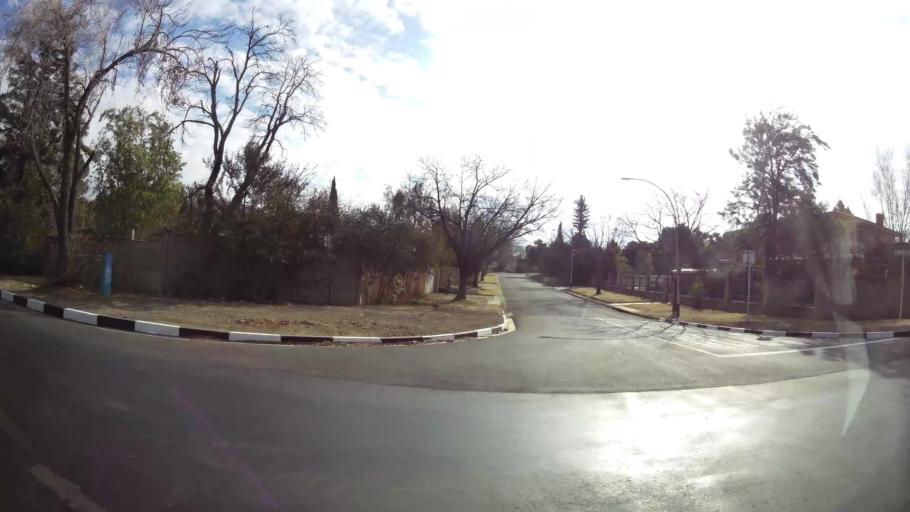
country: ZA
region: Orange Free State
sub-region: Mangaung Metropolitan Municipality
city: Bloemfontein
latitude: -29.0776
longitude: 26.2367
